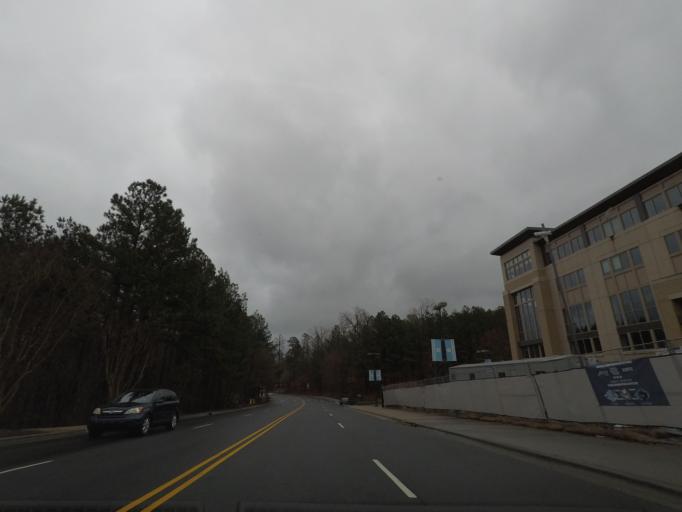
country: US
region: North Carolina
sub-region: Orange County
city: Chapel Hill
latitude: 35.9003
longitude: -79.0425
